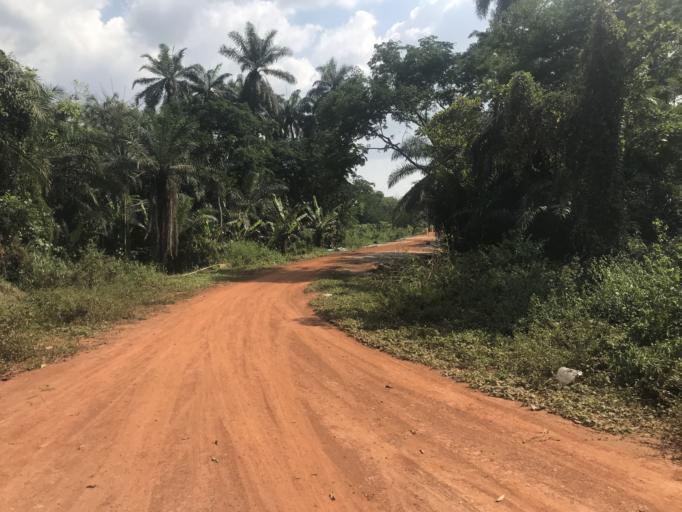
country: NG
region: Osun
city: Ibokun
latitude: 7.8257
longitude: 4.7003
